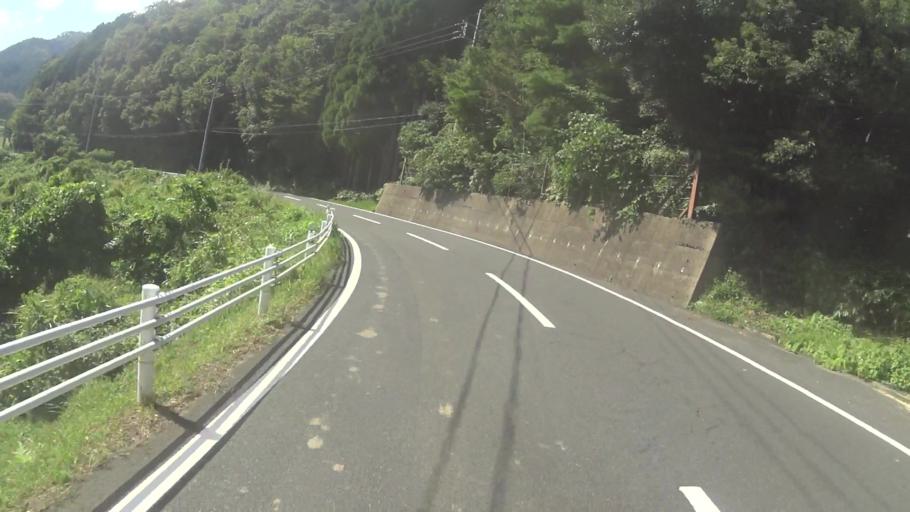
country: JP
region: Kyoto
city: Miyazu
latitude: 35.7098
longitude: 135.2682
